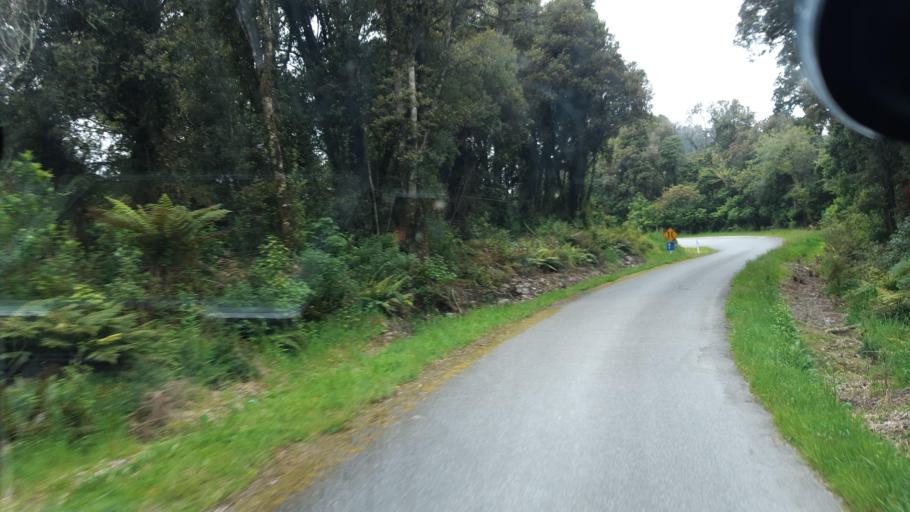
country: NZ
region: West Coast
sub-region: Grey District
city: Greymouth
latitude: -42.6467
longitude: 171.3529
